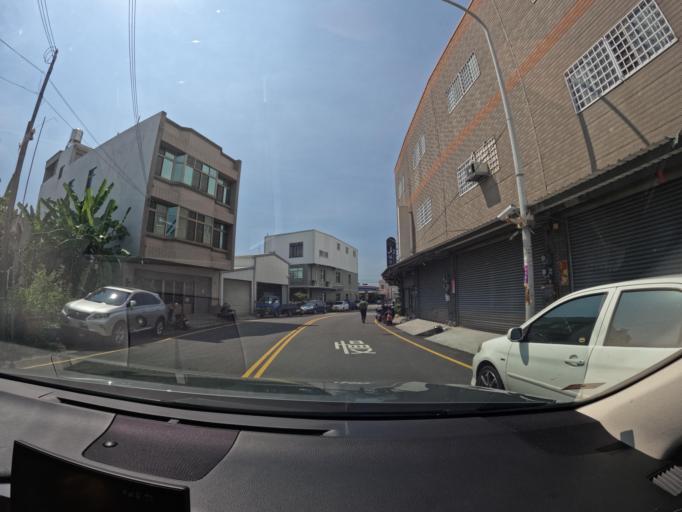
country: TW
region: Taiwan
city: Fengyuan
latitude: 24.3098
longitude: 120.8236
